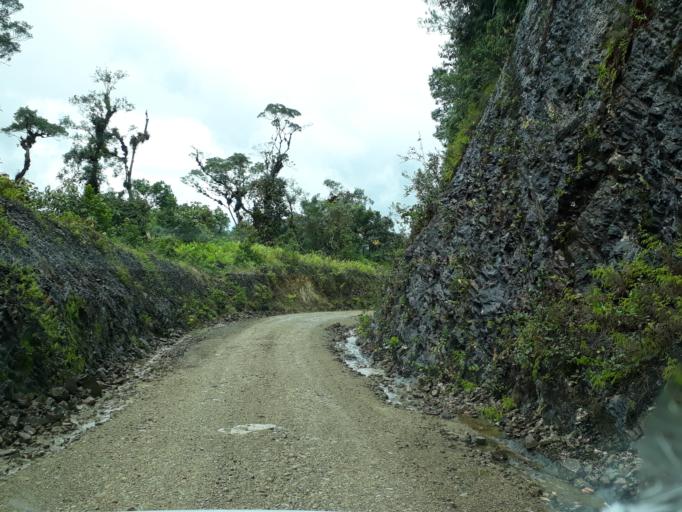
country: CO
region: Cundinamarca
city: Gachala
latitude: 4.7078
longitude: -73.3955
